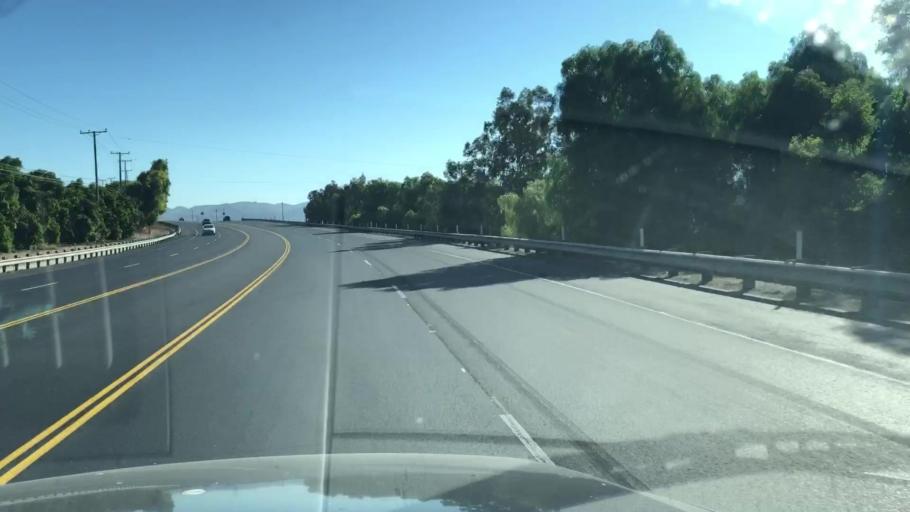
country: US
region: California
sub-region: Ventura County
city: Piru
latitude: 34.3980
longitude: -118.8457
